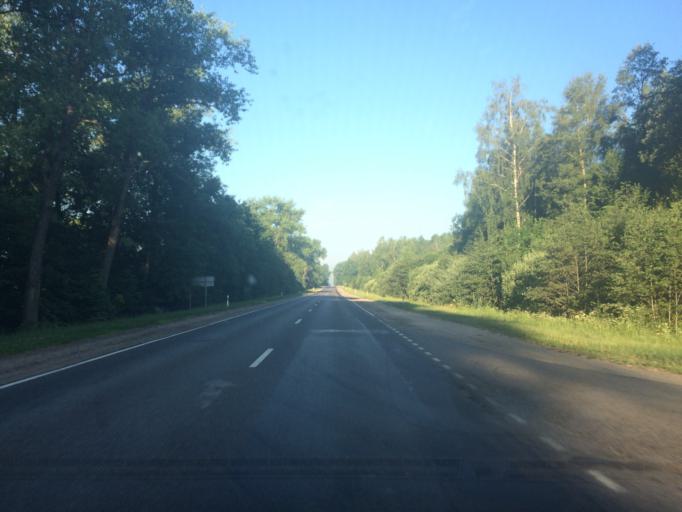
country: LT
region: Utenos apskritis
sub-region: Anyksciai
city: Anyksciai
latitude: 55.3567
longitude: 24.9682
